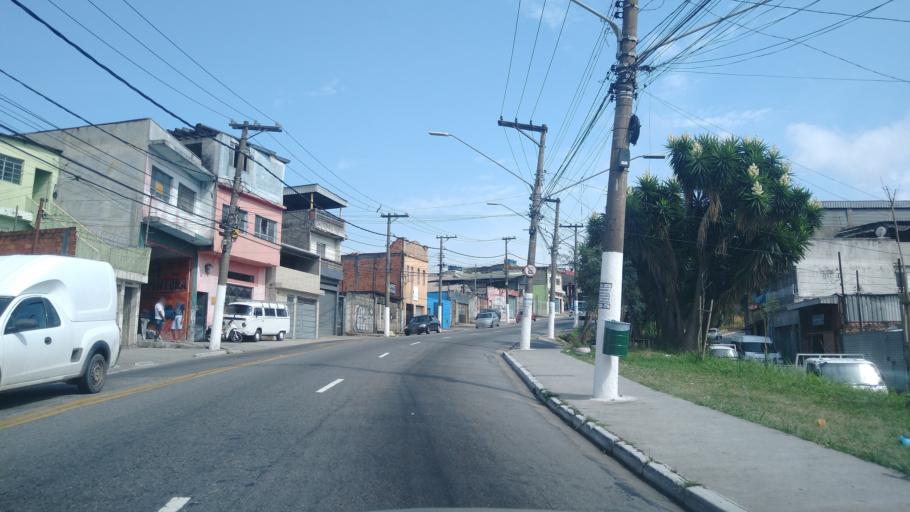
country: BR
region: Sao Paulo
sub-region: Sao Paulo
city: Sao Paulo
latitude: -23.4627
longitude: -46.6834
